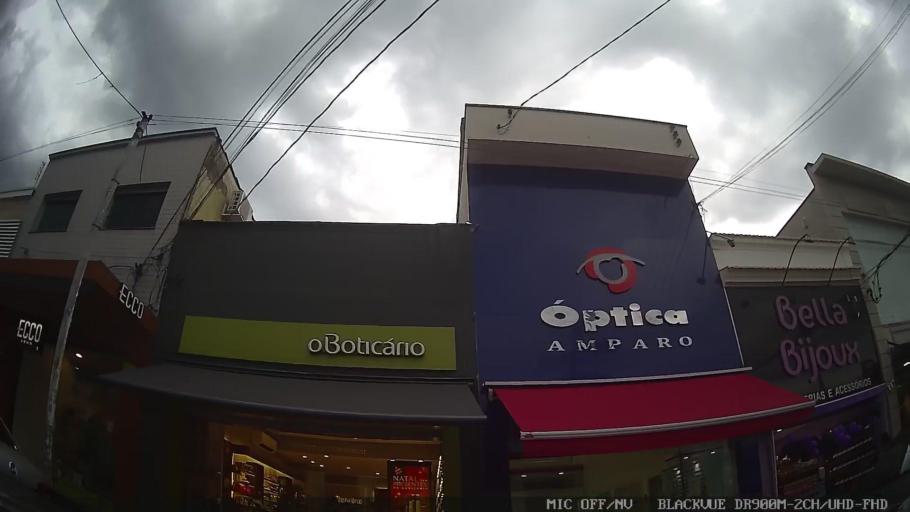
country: BR
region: Sao Paulo
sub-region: Amparo
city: Amparo
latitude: -22.7037
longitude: -46.7680
